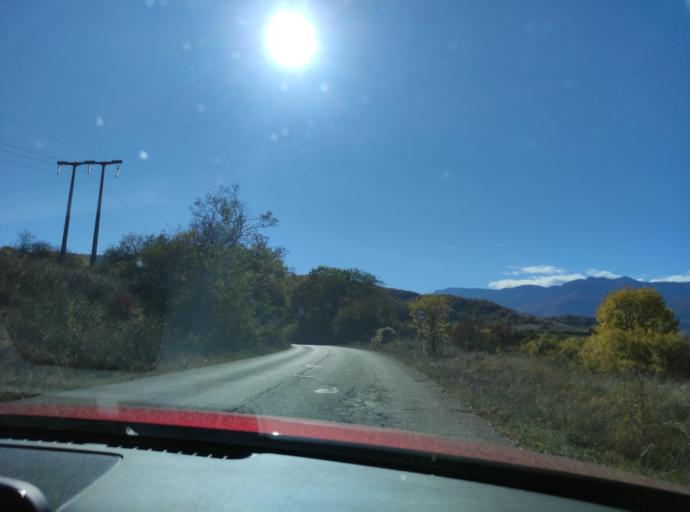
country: BG
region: Montana
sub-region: Obshtina Chiprovtsi
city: Chiprovtsi
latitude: 43.3829
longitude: 22.9189
